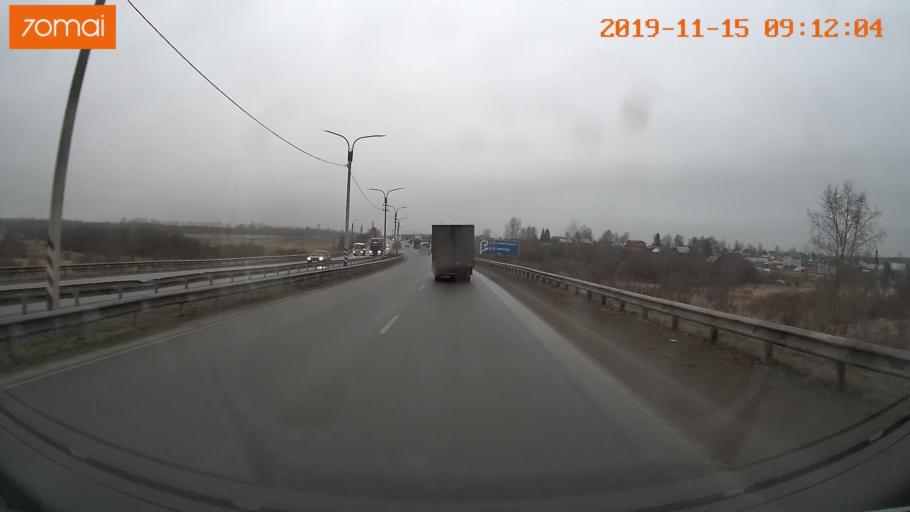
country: RU
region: Vologda
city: Tonshalovo
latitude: 59.2043
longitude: 37.9410
